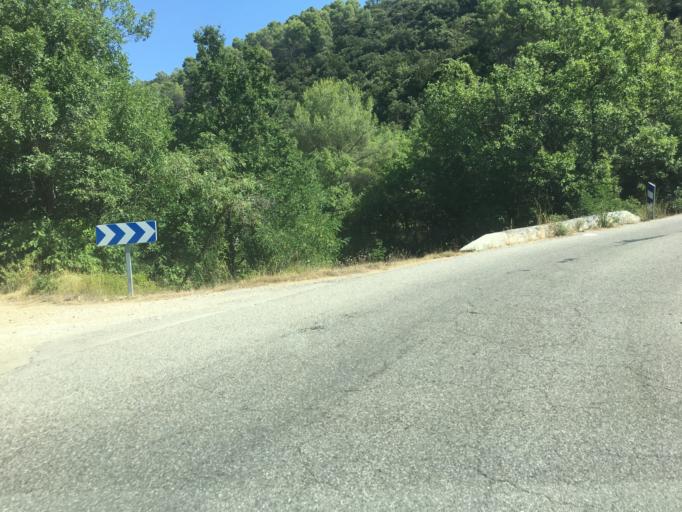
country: FR
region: Provence-Alpes-Cote d'Azur
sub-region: Departement des Alpes-de-Haute-Provence
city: Oraison
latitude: 43.8923
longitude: 5.9550
